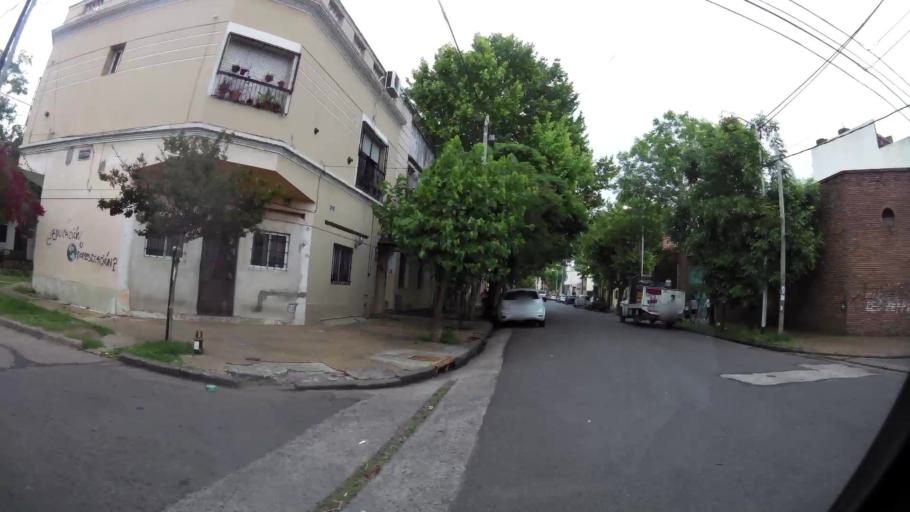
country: AR
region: Buenos Aires
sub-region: Partido de Avellaneda
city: Avellaneda
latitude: -34.6666
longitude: -58.3540
